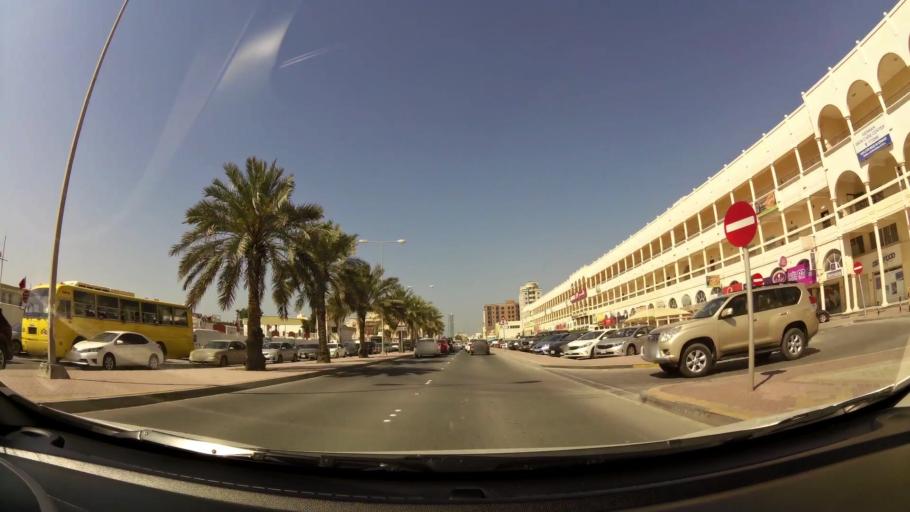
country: BH
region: Manama
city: Manama
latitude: 26.2078
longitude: 50.5756
